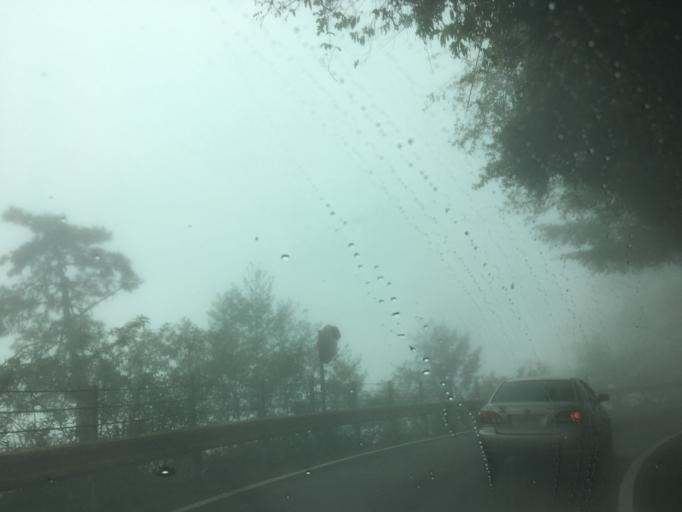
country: TW
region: Taiwan
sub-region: Hualien
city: Hualian
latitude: 24.1868
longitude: 121.4218
